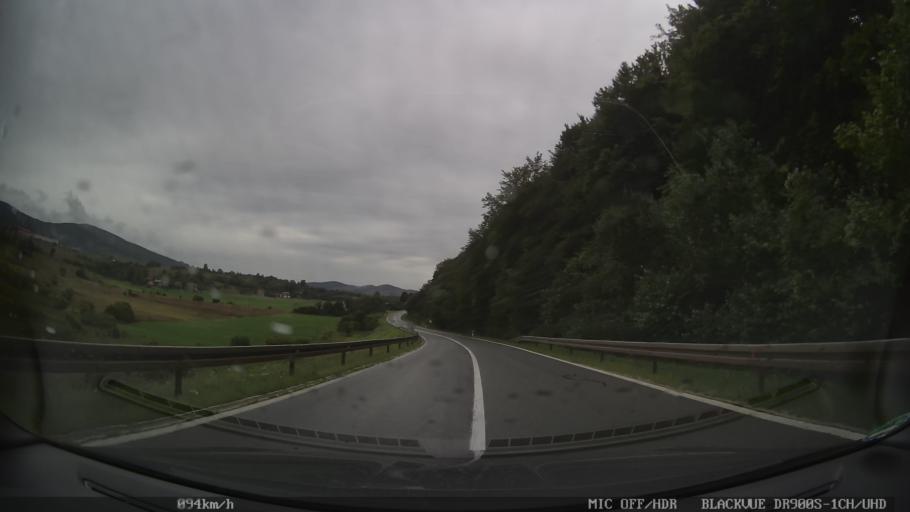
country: HR
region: Licko-Senjska
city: Brinje
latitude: 44.9591
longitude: 15.0934
